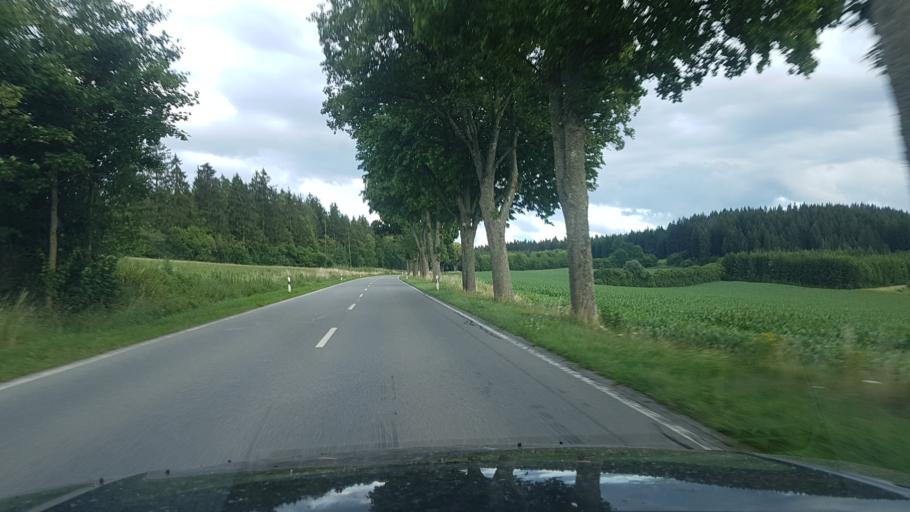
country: DE
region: Baden-Wuerttemberg
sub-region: Freiburg Region
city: Braunlingen
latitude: 47.9654
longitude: 8.4426
